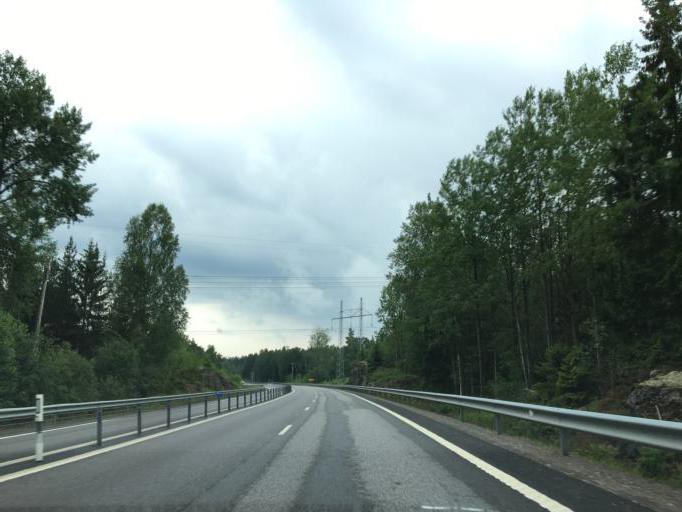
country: SE
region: OEstergoetland
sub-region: Norrkopings Kommun
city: Jursla
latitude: 58.8077
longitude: 16.1514
